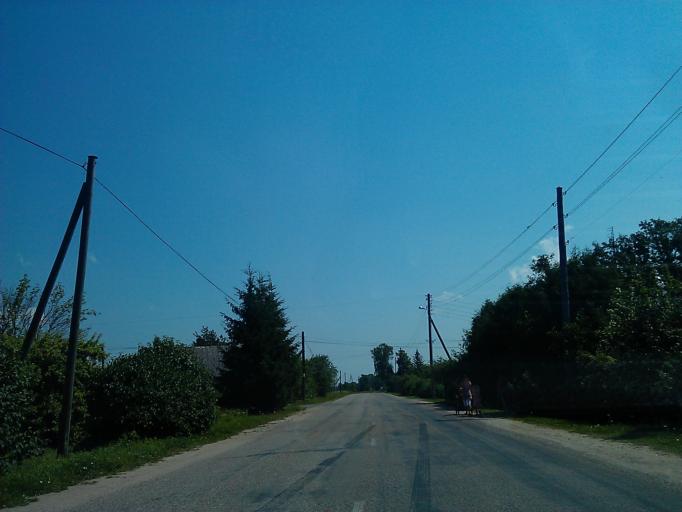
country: LV
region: Aizpute
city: Aizpute
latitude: 56.7182
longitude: 21.6187
